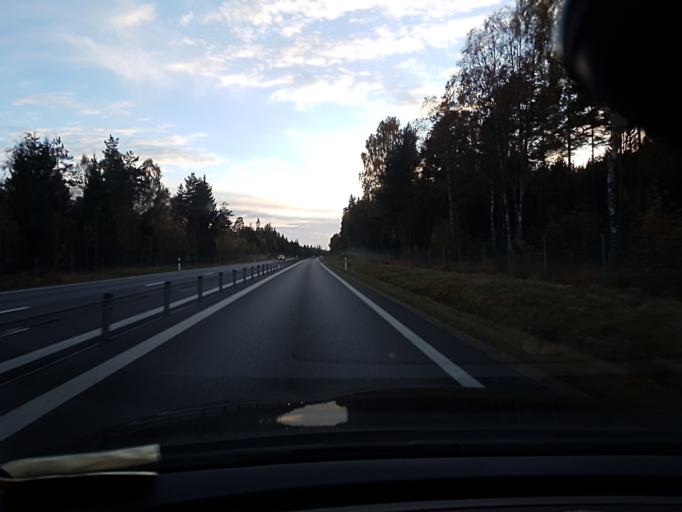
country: SE
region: Kronoberg
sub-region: Ljungby Kommun
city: Ljungby
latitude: 56.7706
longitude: 13.8044
